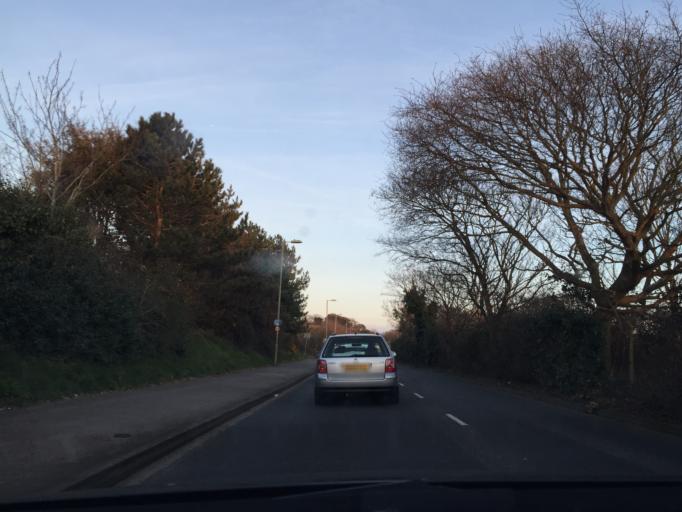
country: GB
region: England
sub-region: Hampshire
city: Lee-on-the-Solent
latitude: 50.7884
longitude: -1.1703
